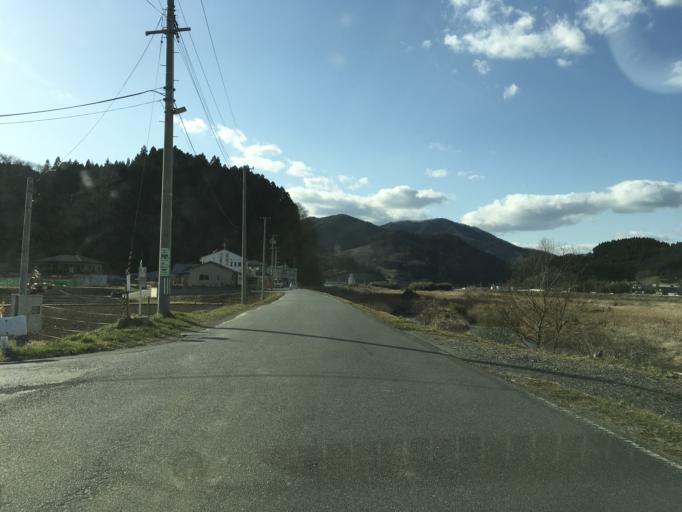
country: JP
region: Iwate
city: Ofunato
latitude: 39.0281
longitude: 141.6116
